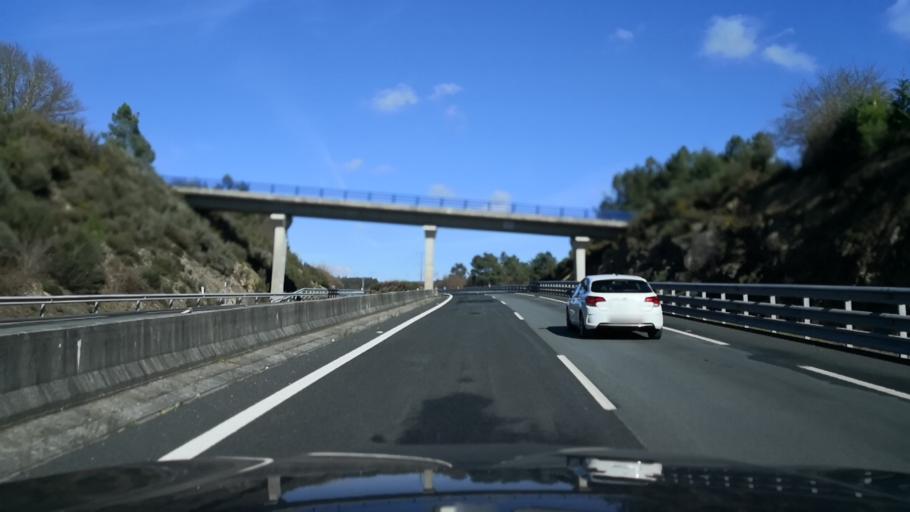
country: ES
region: Galicia
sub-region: Provincia de Ourense
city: Pinor
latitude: 42.5034
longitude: -8.0259
